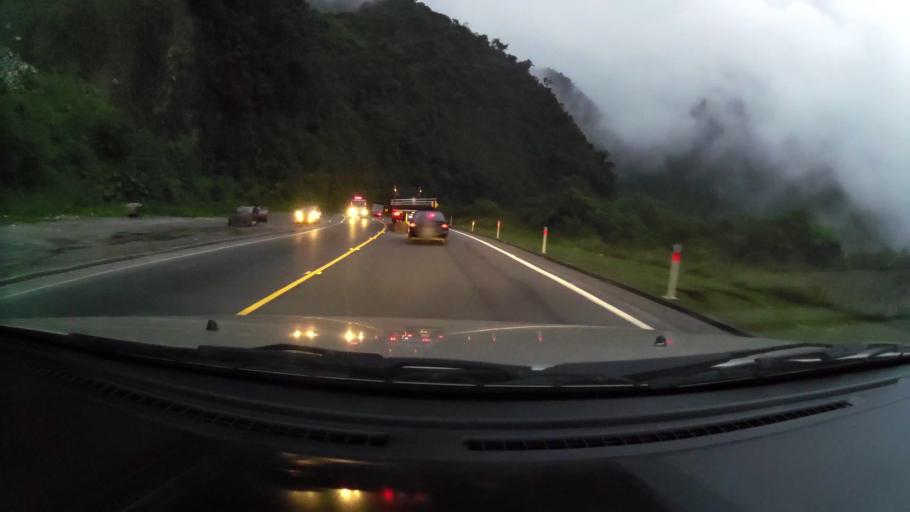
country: EC
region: Pichincha
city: Machachi
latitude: -0.4469
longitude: -78.6841
